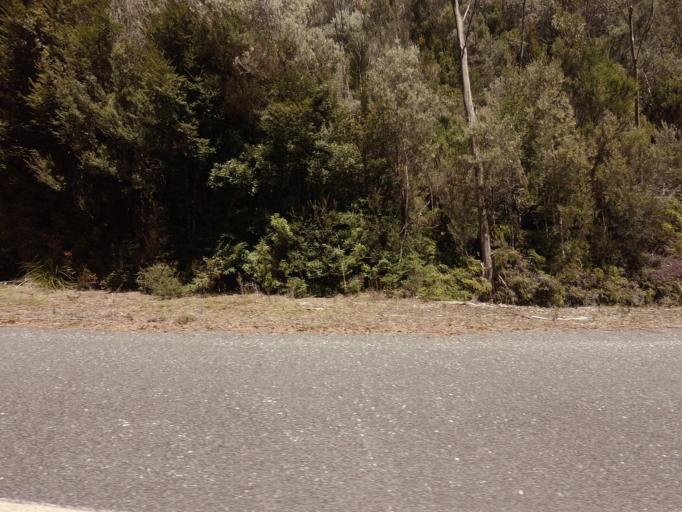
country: AU
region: Tasmania
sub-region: West Coast
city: Queenstown
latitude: -42.7690
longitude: 146.0075
